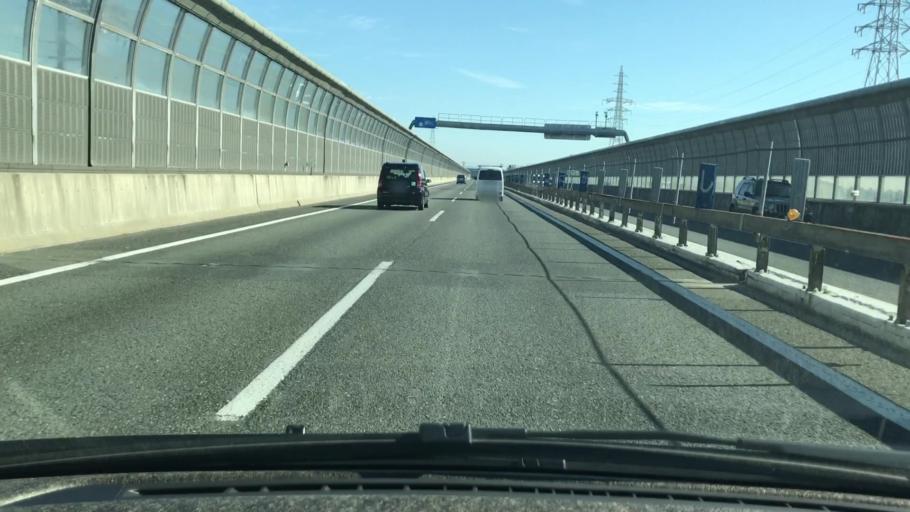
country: JP
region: Hyogo
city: Amagasaki
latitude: 34.7442
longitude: 135.4375
